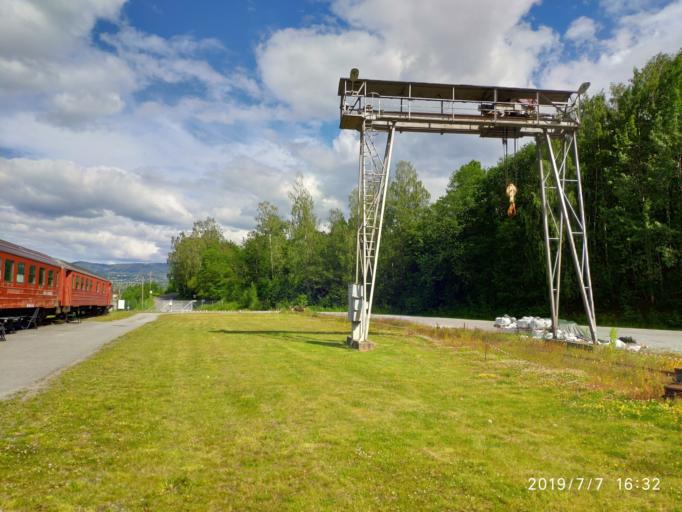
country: NO
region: Buskerud
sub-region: Ringerike
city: Honefoss
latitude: 60.1684
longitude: 10.2440
